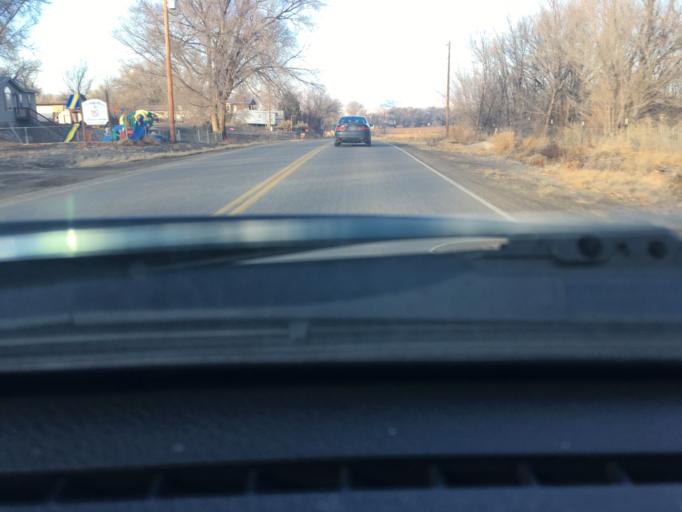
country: US
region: Colorado
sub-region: Delta County
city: Delta
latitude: 38.7410
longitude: -108.0931
